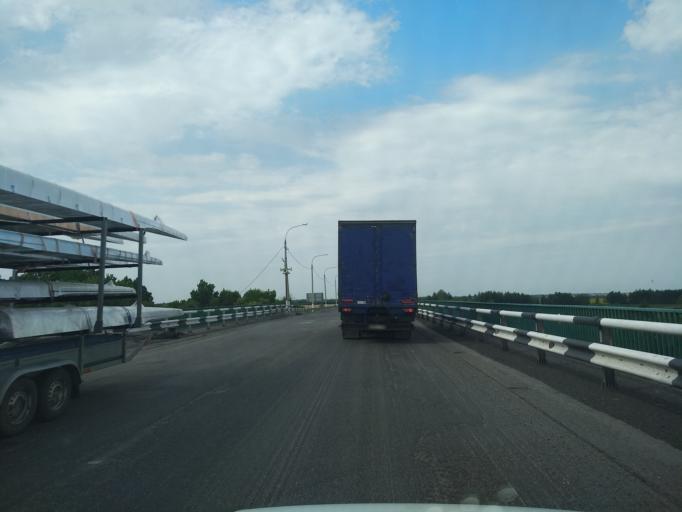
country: RU
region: Voronezj
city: Pereleshino
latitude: 51.7619
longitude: 40.1267
